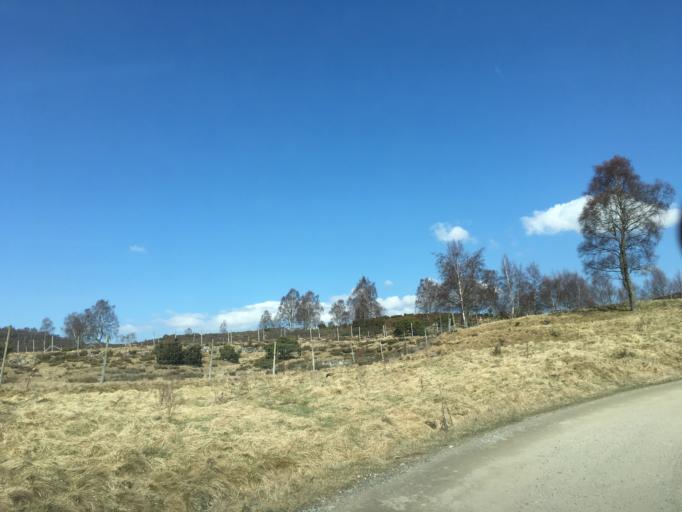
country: GB
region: Scotland
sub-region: Highland
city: Kingussie
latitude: 57.1139
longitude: -3.9818
